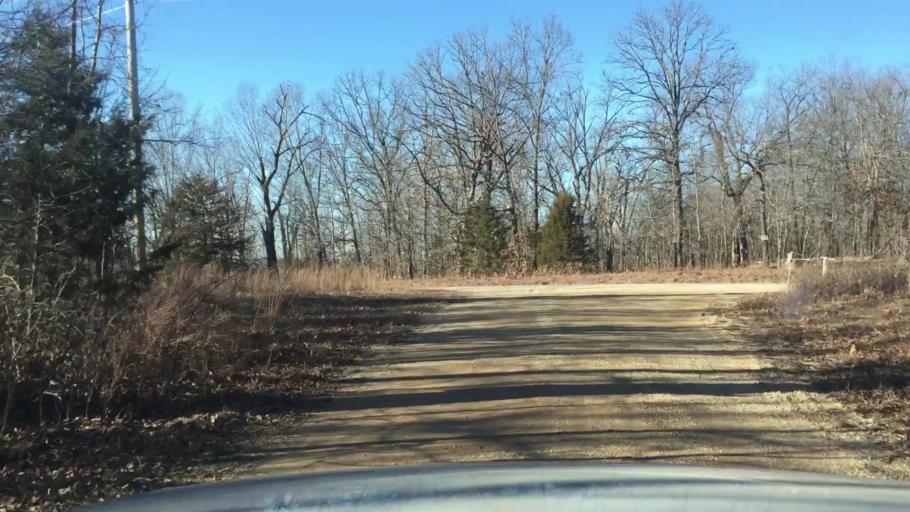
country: US
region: Missouri
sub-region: Morgan County
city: Versailles
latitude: 38.3308
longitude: -92.7721
